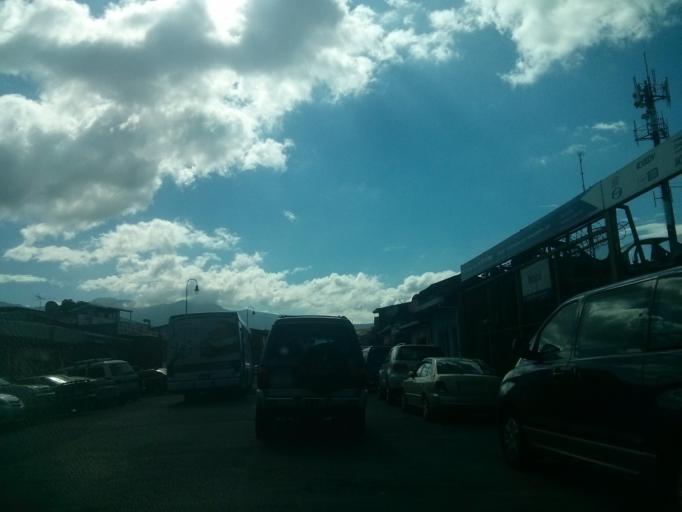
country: CR
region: San Jose
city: San Jose
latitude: 9.9289
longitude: -84.0846
